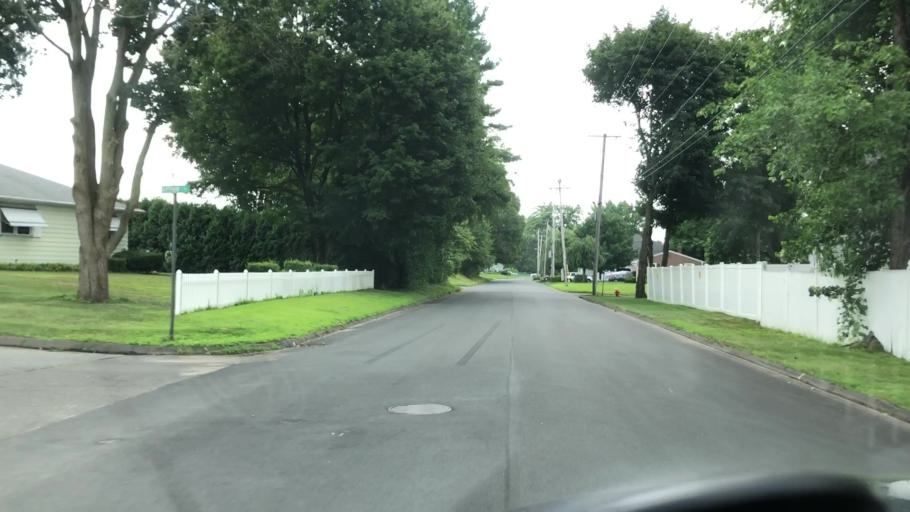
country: US
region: Massachusetts
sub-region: Hampden County
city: Chicopee
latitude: 42.1602
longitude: -72.6215
